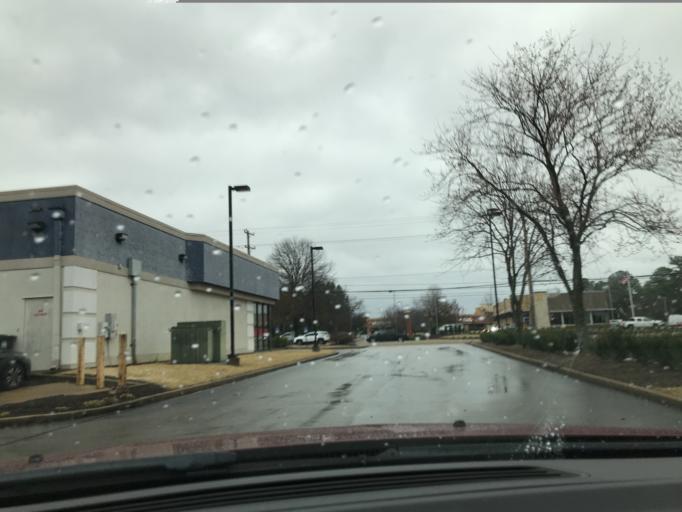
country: US
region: Tennessee
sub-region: Shelby County
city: Collierville
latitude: 35.0455
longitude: -89.6911
